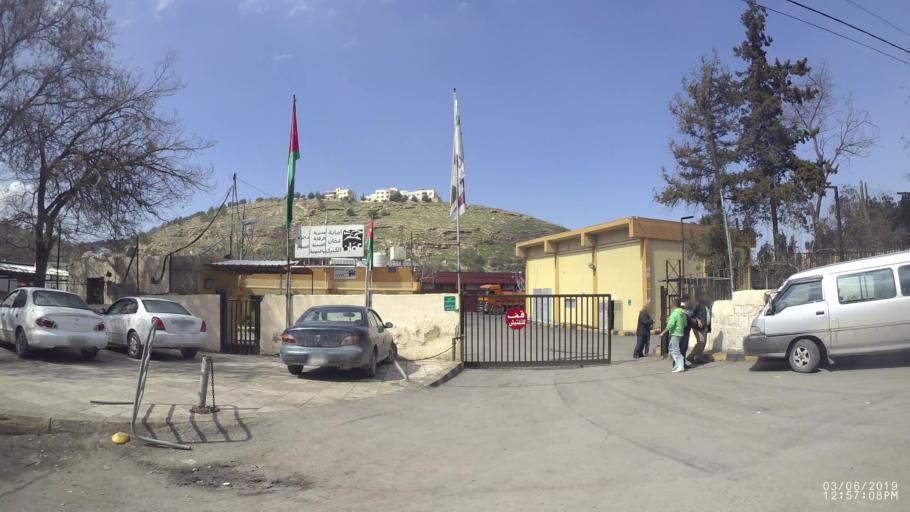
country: JO
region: Amman
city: Amman
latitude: 31.9805
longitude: 35.9755
